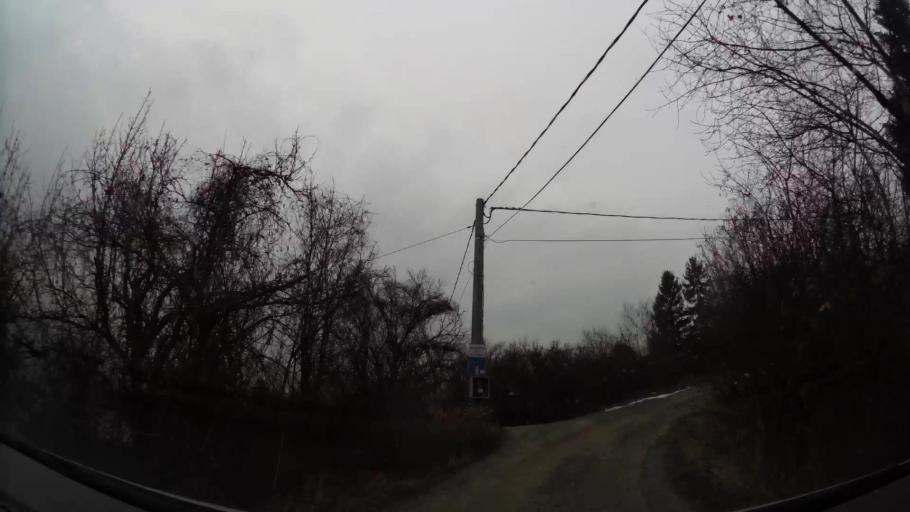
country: BG
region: Sofia-Capital
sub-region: Stolichna Obshtina
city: Sofia
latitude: 42.5986
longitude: 23.3954
